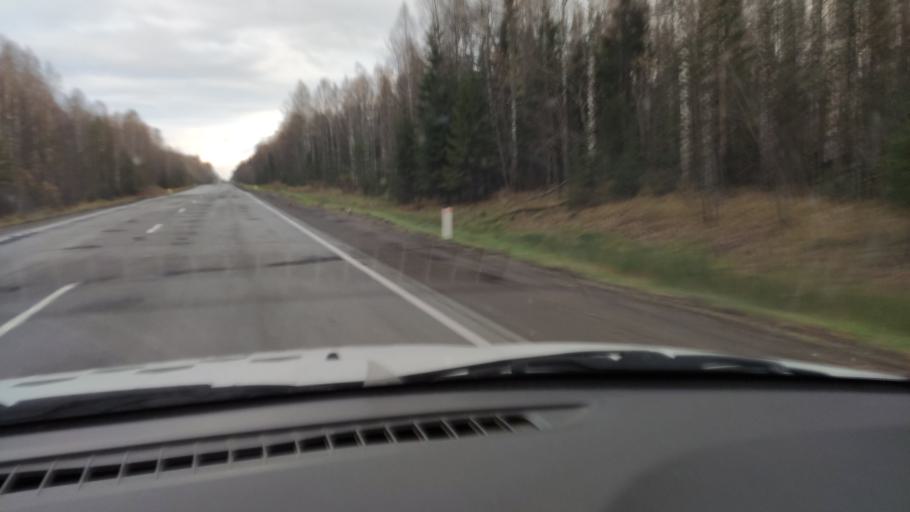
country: RU
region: Kirov
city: Omutninsk
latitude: 58.7666
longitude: 51.9776
